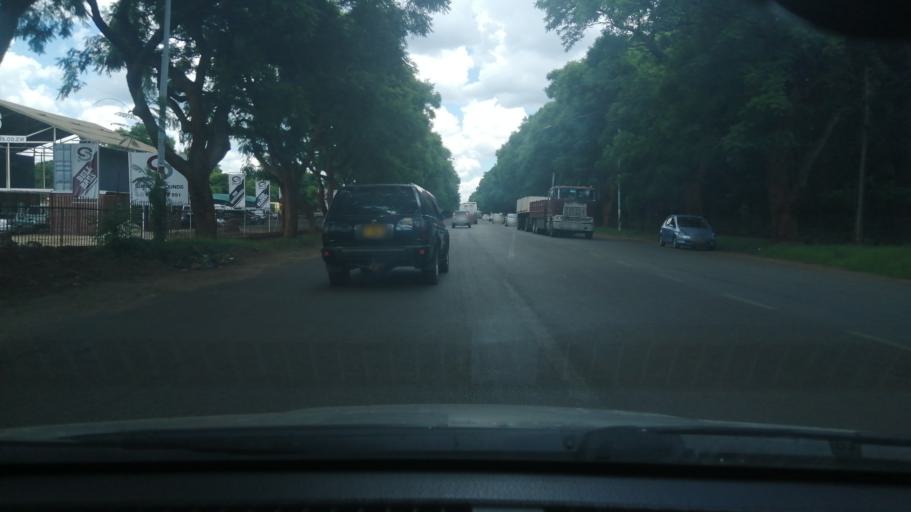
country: ZW
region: Harare
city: Harare
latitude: -17.8195
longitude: 31.0325
